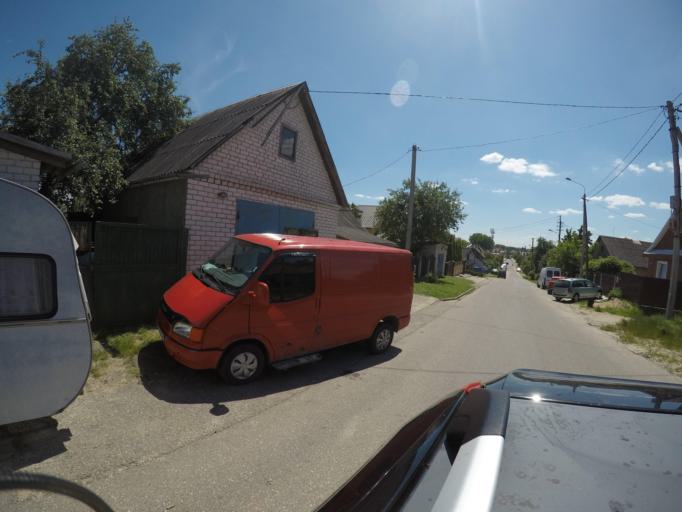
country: BY
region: Grodnenskaya
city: Hrodna
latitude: 53.6916
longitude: 23.8178
